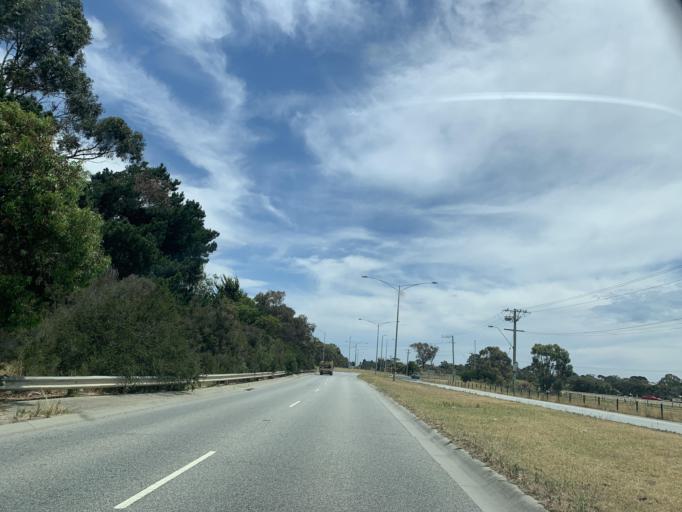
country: AU
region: Victoria
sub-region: Casey
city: Cranbourne South
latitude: -38.1332
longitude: 145.2301
